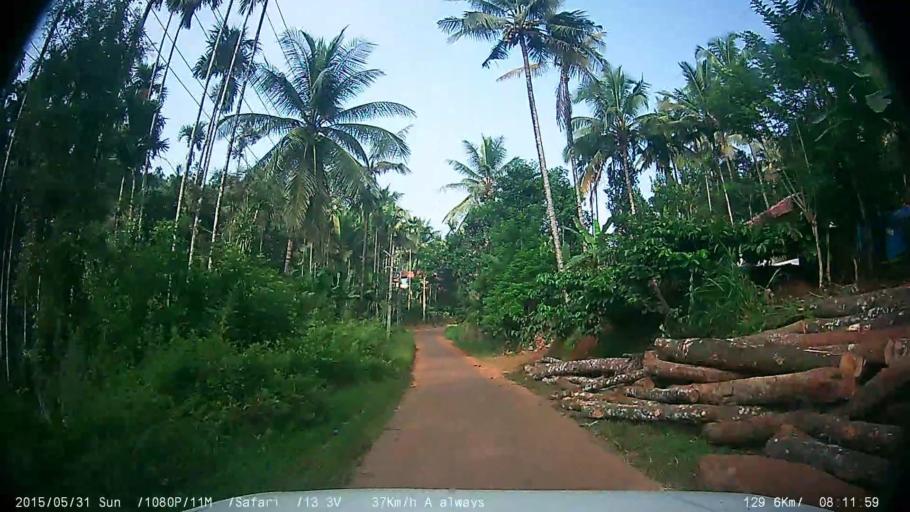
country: IN
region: Kerala
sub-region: Wayanad
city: Kalpetta
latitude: 11.6377
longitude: 76.0151
